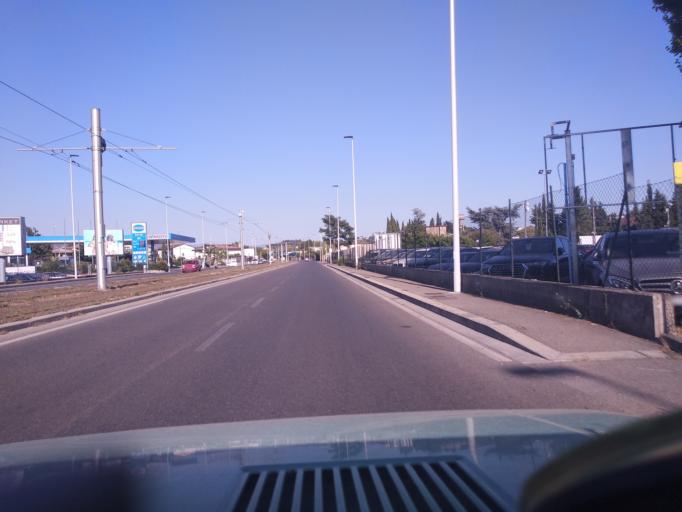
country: IT
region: Tuscany
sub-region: Province of Florence
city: Scandicci
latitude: 43.7645
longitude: 11.2013
